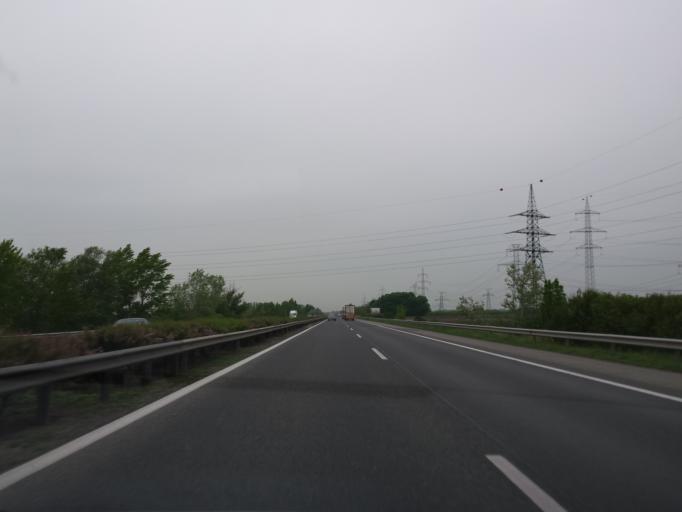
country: HU
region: Gyor-Moson-Sopron
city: Gyor
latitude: 47.6584
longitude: 17.5934
